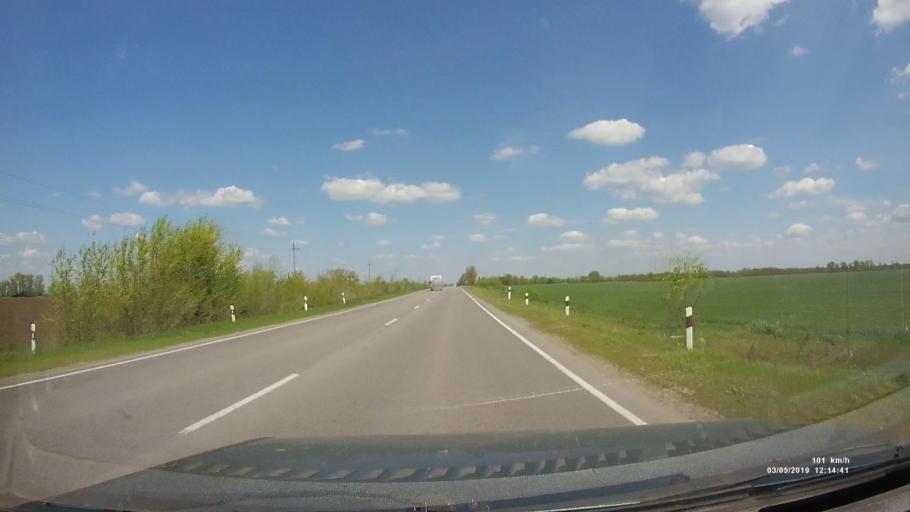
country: RU
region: Rostov
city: Melikhovskaya
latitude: 47.3473
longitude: 40.5659
